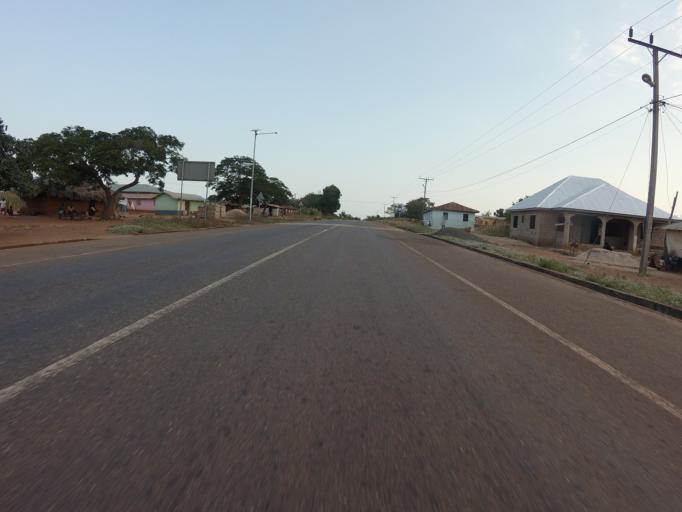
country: GH
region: Volta
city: Anloga
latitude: 6.0741
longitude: 0.6044
